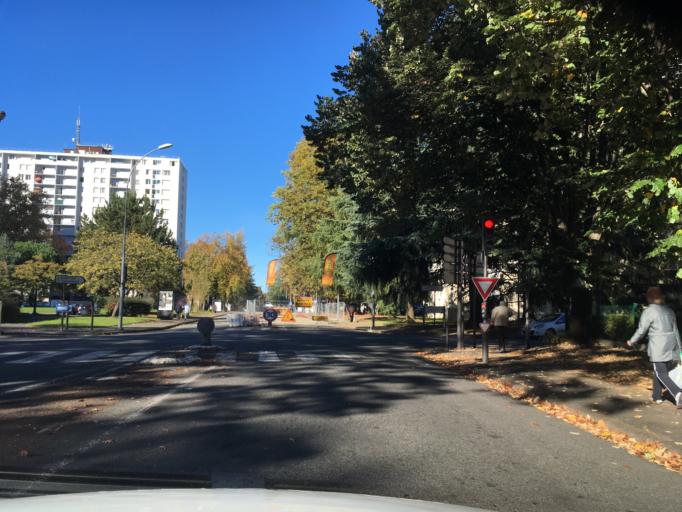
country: FR
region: Aquitaine
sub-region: Departement des Pyrenees-Atlantiques
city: Pau
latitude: 43.3076
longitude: -0.3562
